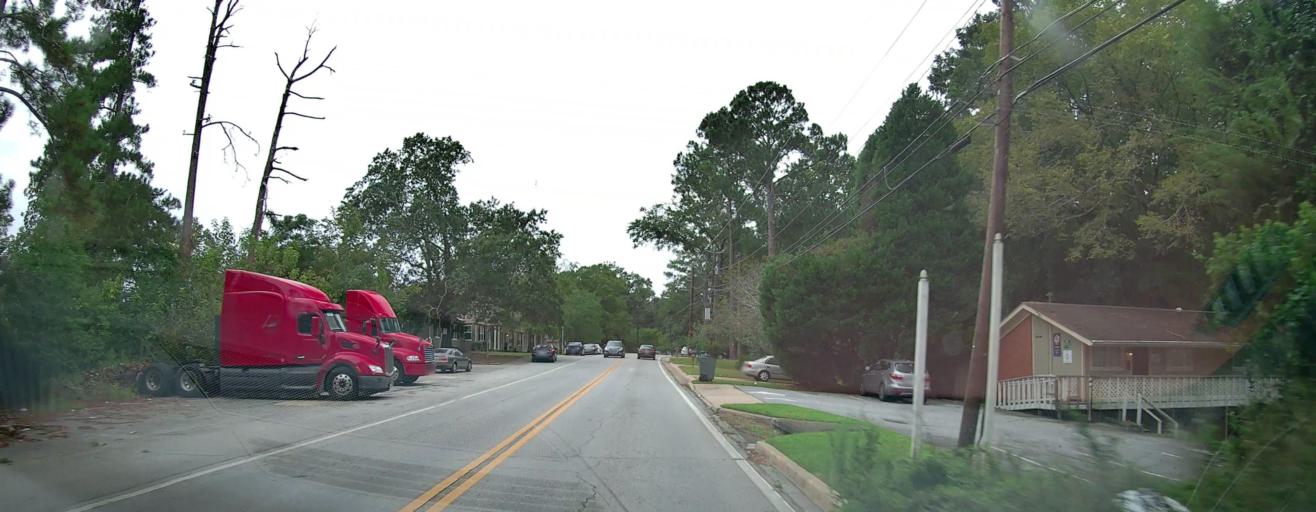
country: US
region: Georgia
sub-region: Bibb County
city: Macon
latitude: 32.8544
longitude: -83.6486
